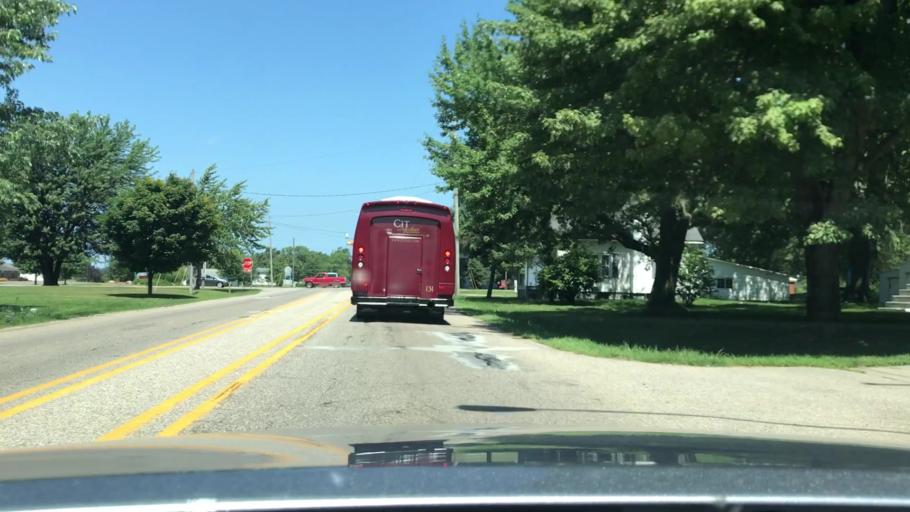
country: US
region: Michigan
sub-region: Ottawa County
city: Zeeland
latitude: 42.8845
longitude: -86.0803
